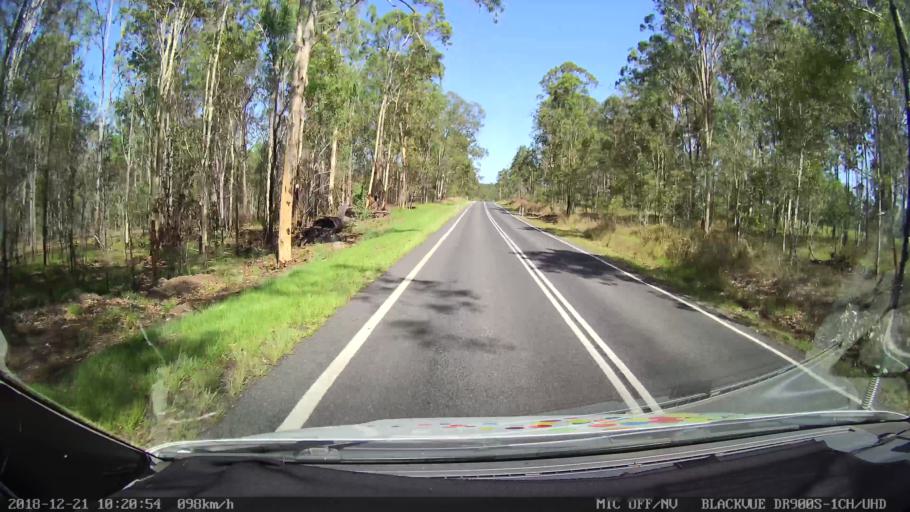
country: AU
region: New South Wales
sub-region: Clarence Valley
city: South Grafton
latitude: -29.6642
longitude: 152.8216
